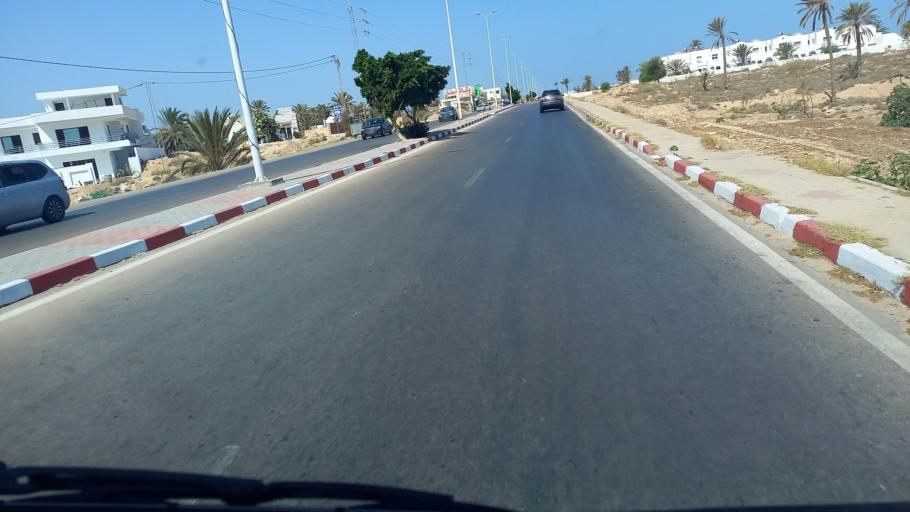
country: TN
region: Madanin
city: Midoun
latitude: 33.8605
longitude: 10.9702
